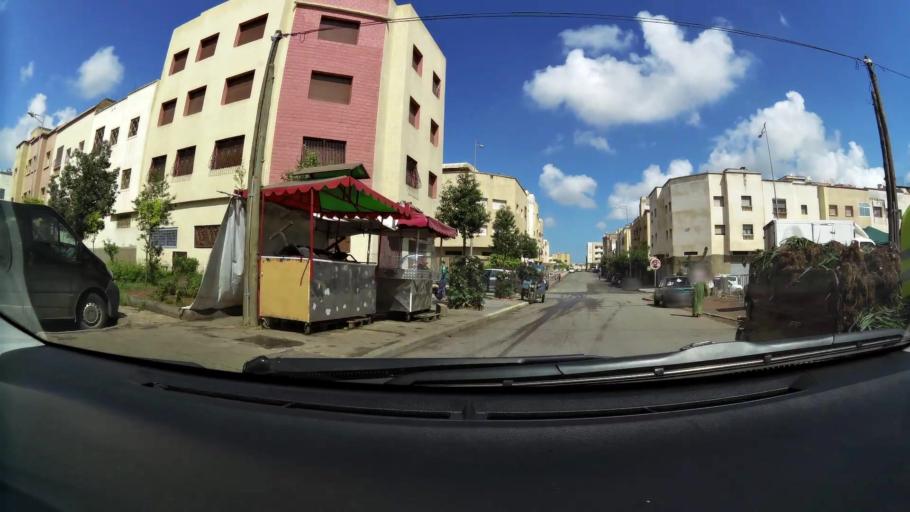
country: MA
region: Grand Casablanca
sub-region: Mediouna
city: Tit Mellil
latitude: 33.5493
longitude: -7.4841
